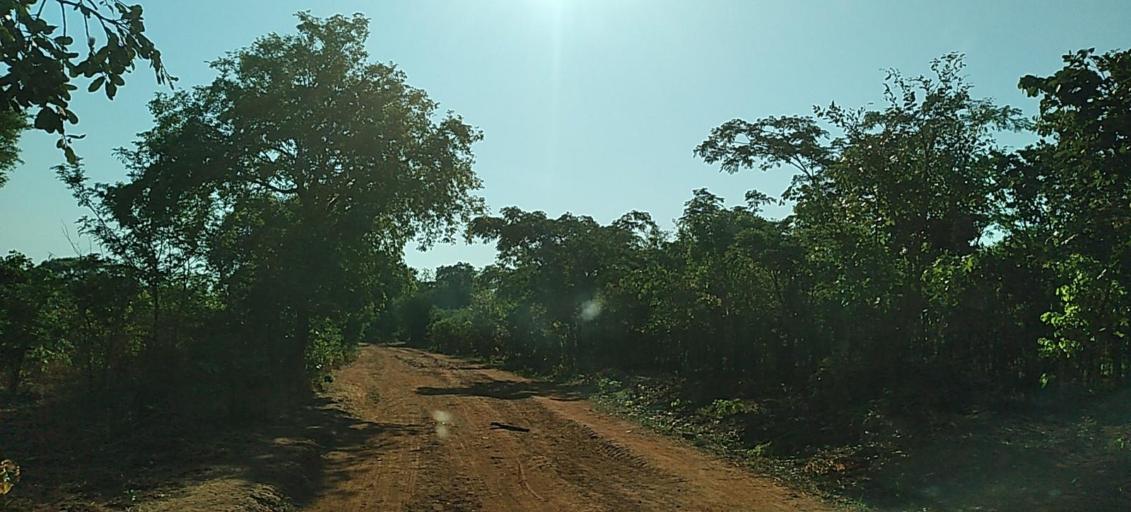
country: ZM
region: Copperbelt
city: Luanshya
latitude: -13.4592
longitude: 28.8148
